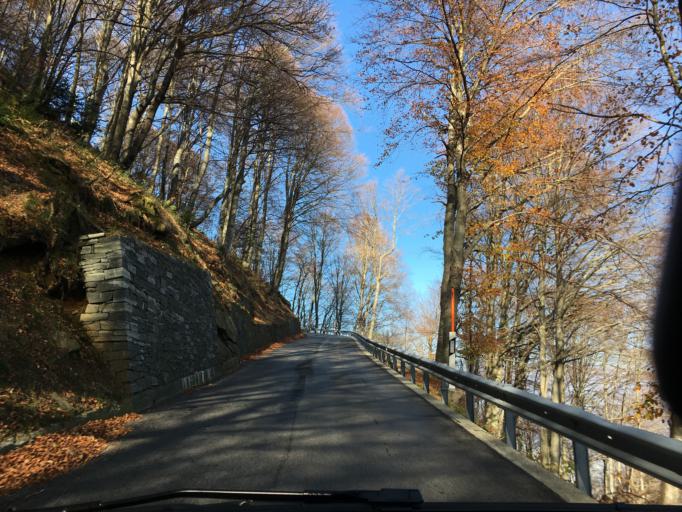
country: CH
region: Ticino
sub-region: Locarno District
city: Magadino
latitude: 46.1182
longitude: 8.8481
